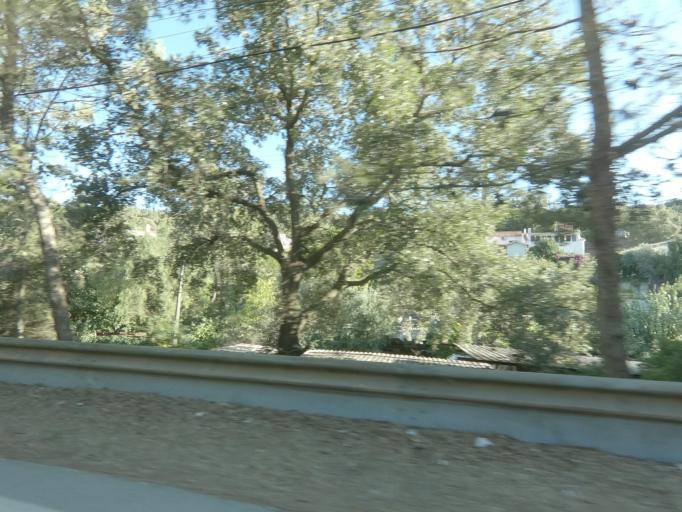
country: PT
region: Setubal
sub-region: Palmela
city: Quinta do Anjo
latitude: 38.5046
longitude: -8.9533
